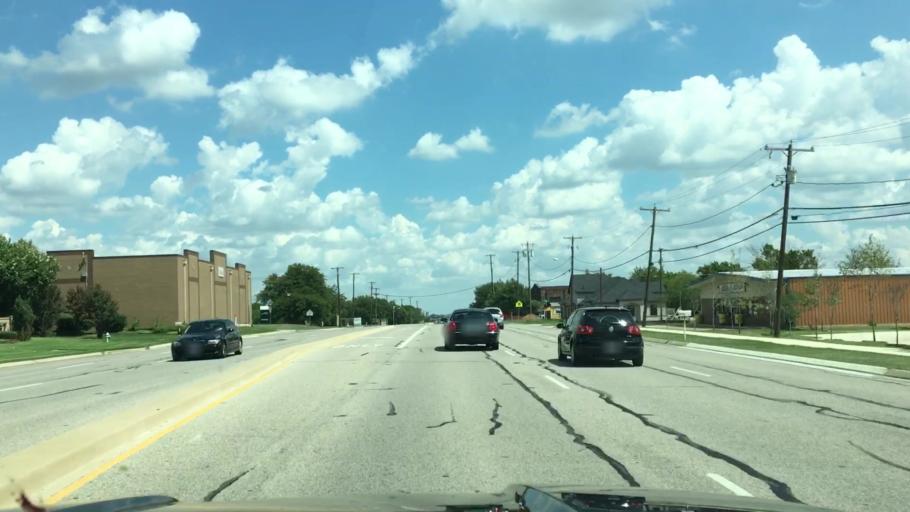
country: US
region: Texas
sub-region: Tarrant County
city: Keller
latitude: 32.9345
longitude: -97.2506
